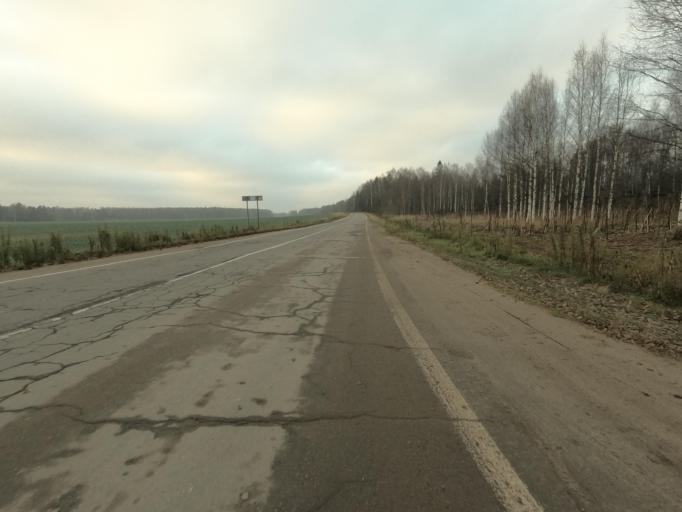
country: RU
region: Leningrad
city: Mga
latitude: 59.7952
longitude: 31.0059
